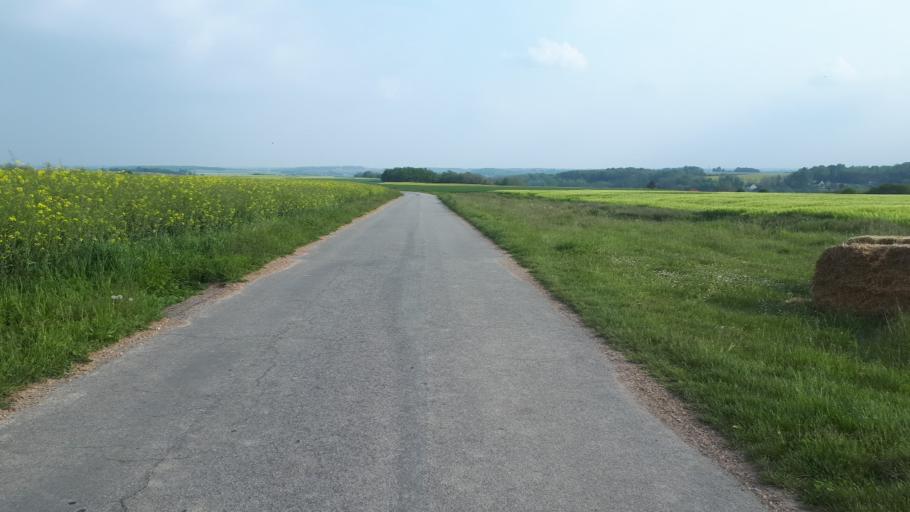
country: FR
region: Centre
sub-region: Departement du Loir-et-Cher
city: Lunay
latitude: 47.8307
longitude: 0.9482
